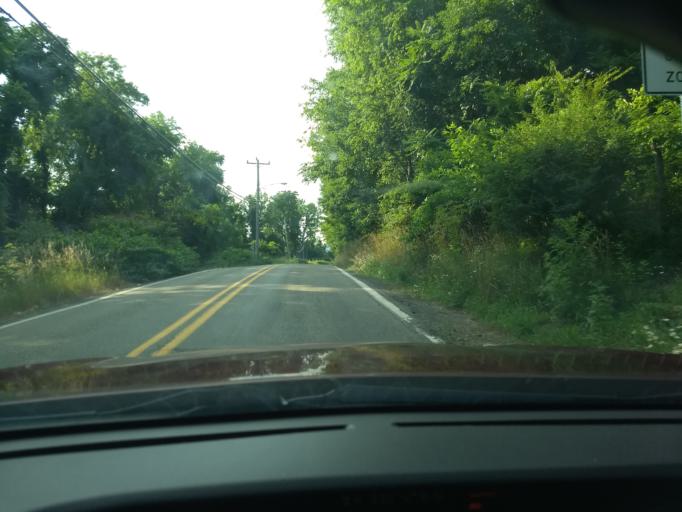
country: US
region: Pennsylvania
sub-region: Westmoreland County
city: Lower Burrell
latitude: 40.5292
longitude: -79.7559
